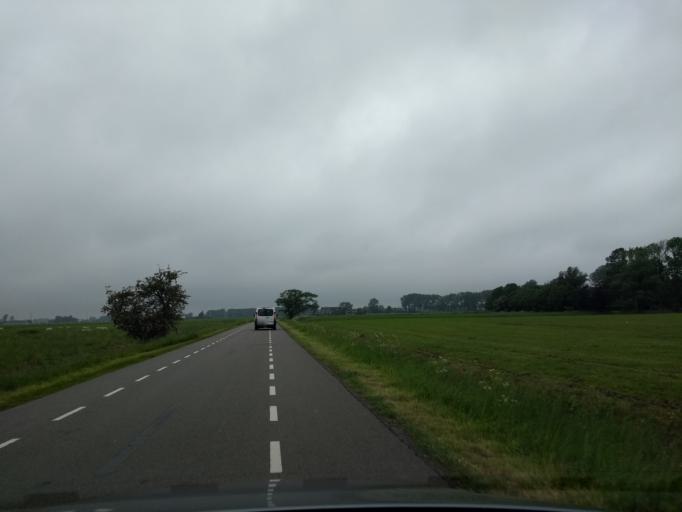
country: NL
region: Groningen
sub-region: Gemeente Zuidhorn
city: Aduard
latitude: 53.2521
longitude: 6.5114
